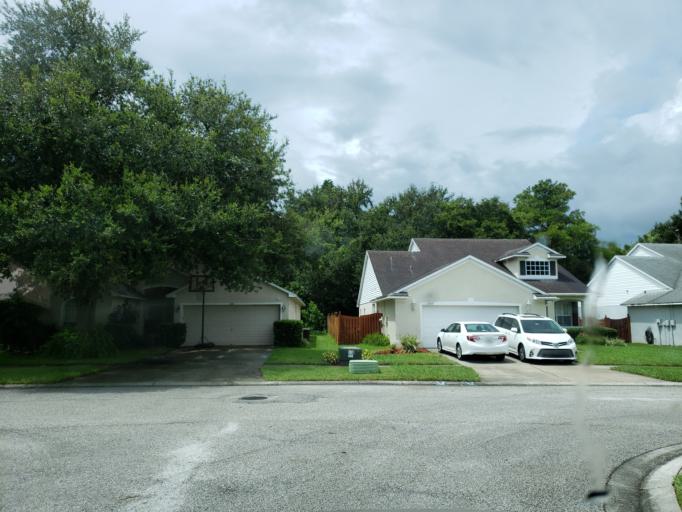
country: US
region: Florida
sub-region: Hillsborough County
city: Bloomingdale
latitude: 27.8979
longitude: -82.2134
